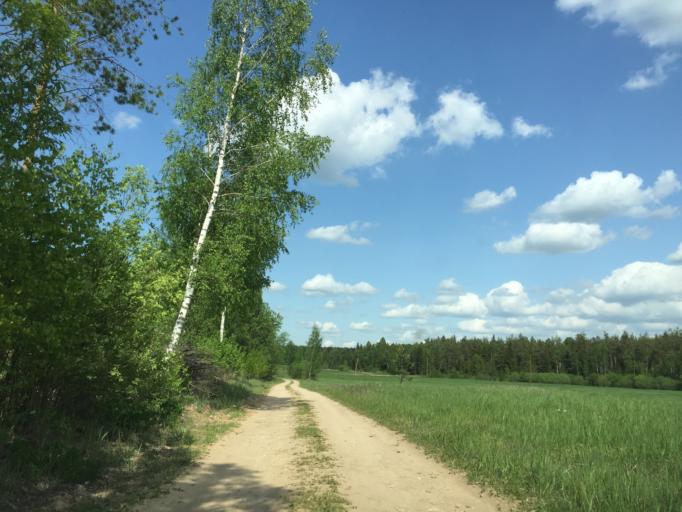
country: LV
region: Baldone
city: Baldone
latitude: 56.7910
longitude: 24.4182
